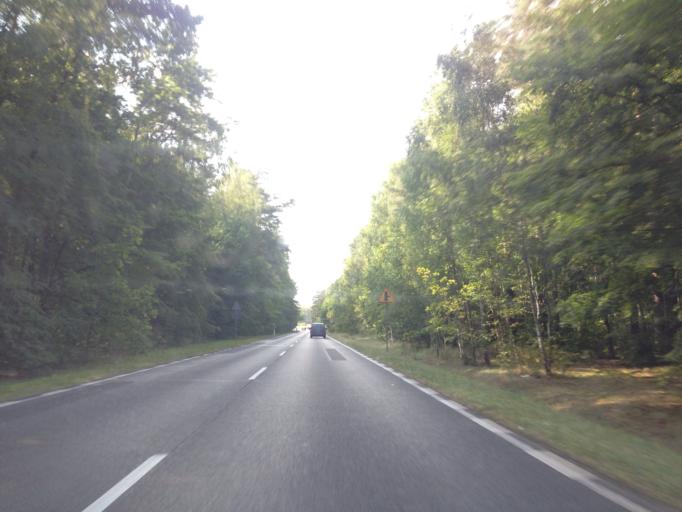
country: PL
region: Kujawsko-Pomorskie
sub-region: Powiat swiecki
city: Swiekatowo
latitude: 53.4835
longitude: 18.1308
